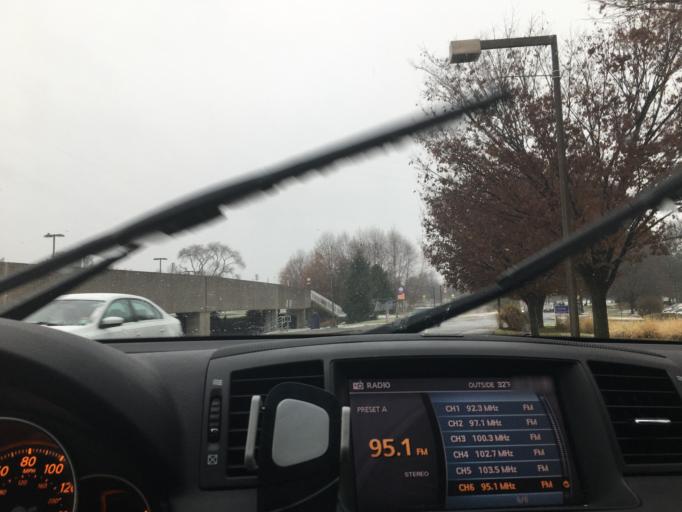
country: US
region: New Jersey
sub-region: Bergen County
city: Paramus
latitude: 40.9517
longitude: -74.0908
